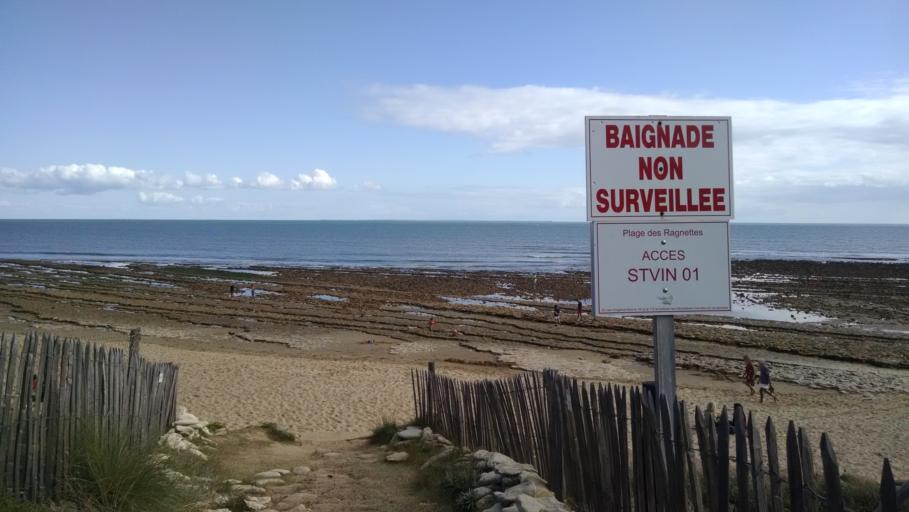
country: FR
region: Pays de la Loire
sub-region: Departement de la Vendee
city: Jard-sur-Mer
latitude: 46.4069
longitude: -1.5585
